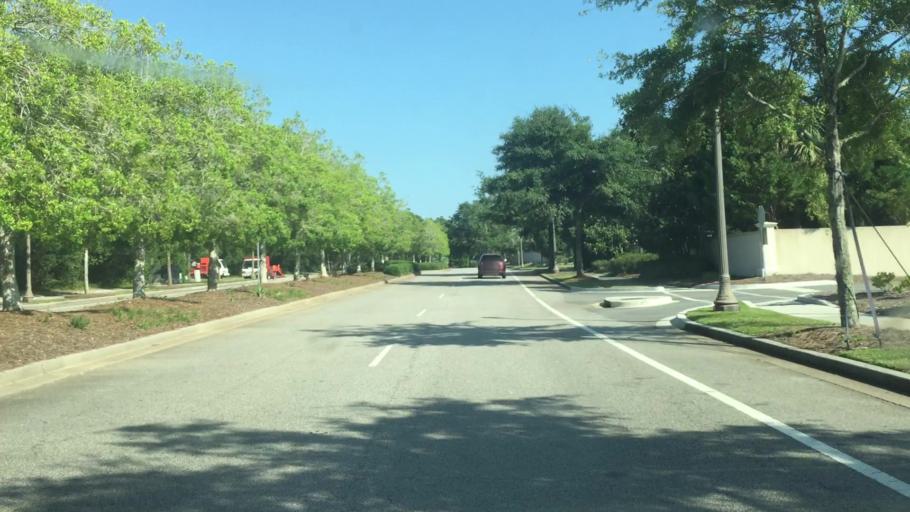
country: US
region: South Carolina
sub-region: Horry County
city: Myrtle Beach
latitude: 33.7508
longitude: -78.8129
